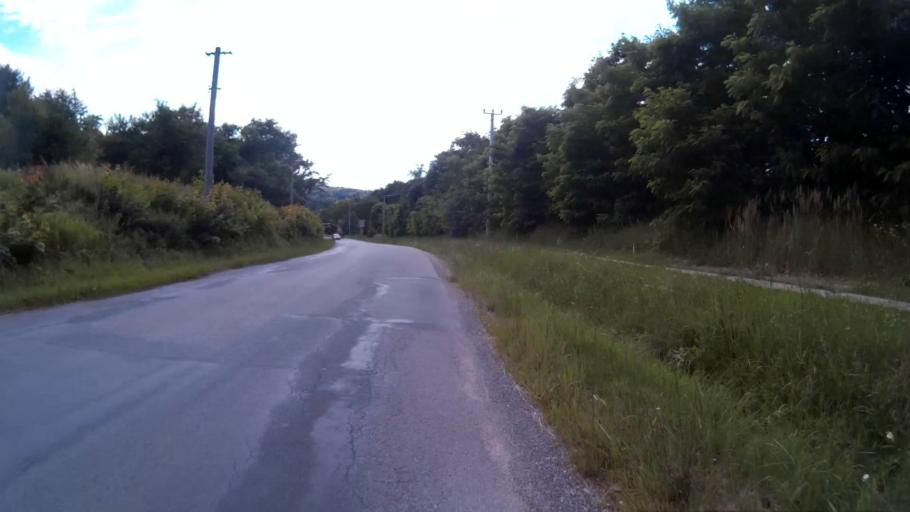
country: CZ
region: South Moravian
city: Strelice
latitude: 49.1531
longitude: 16.4752
